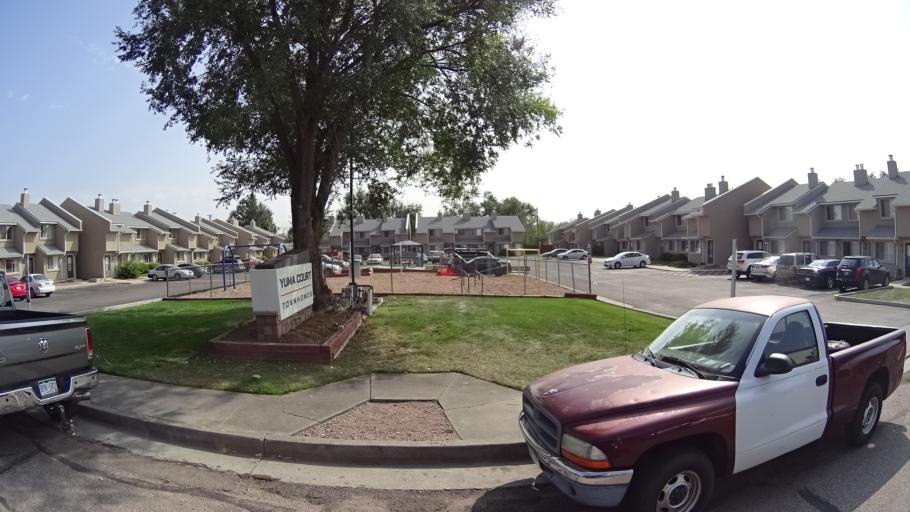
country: US
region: Colorado
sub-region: El Paso County
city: Colorado Springs
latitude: 38.8447
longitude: -104.7781
